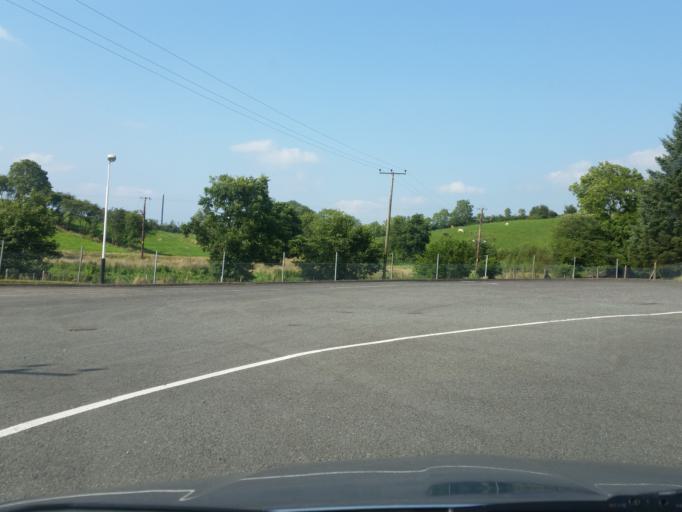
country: GB
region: Northern Ireland
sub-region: Fermanagh District
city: Enniskillen
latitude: 54.3562
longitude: -7.6166
